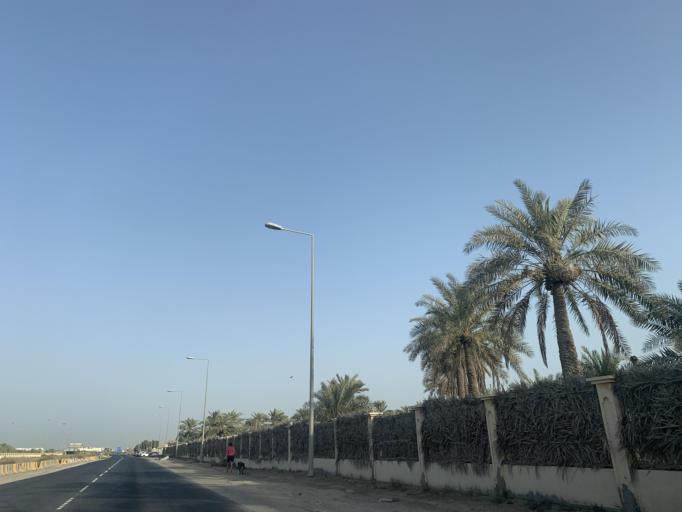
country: BH
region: Central Governorate
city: Madinat Hamad
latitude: 26.1755
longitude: 50.4588
